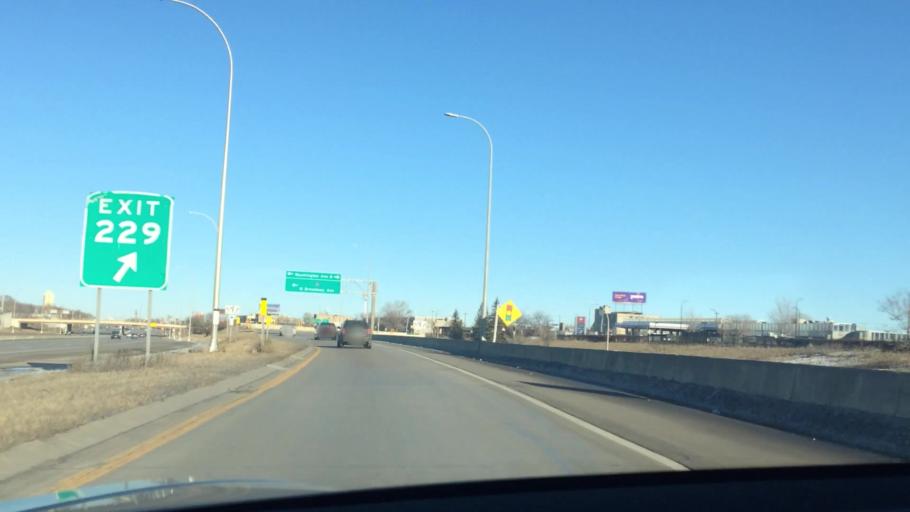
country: US
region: Minnesota
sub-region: Hennepin County
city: Minneapolis
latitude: 44.9942
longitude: -93.2830
